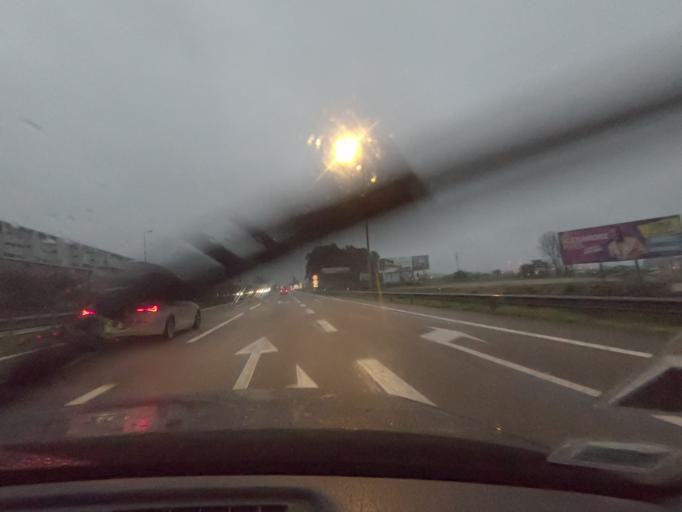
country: PT
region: Porto
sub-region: Matosinhos
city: Santa Cruz do Bispo
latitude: 41.2311
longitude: -8.6956
